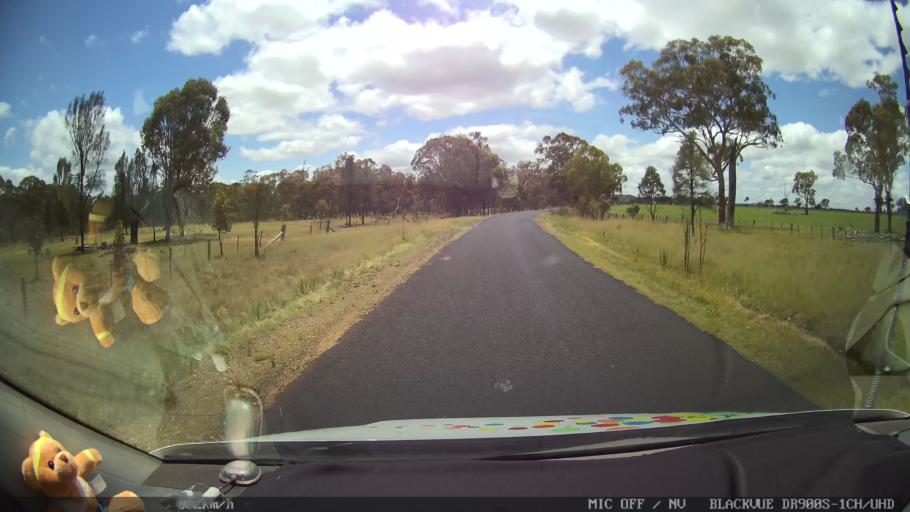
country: AU
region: New South Wales
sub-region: Glen Innes Severn
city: Glen Innes
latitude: -29.4203
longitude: 151.7162
